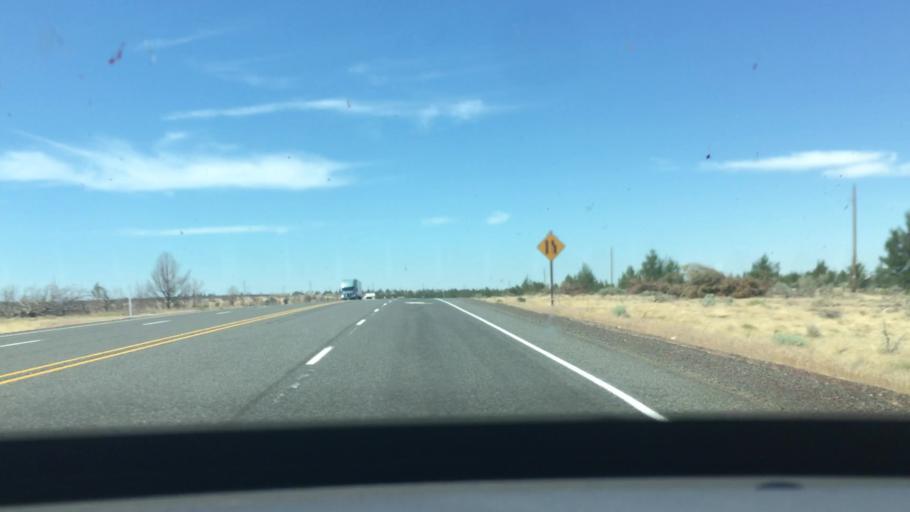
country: US
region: Oregon
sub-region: Jefferson County
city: Madras
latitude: 44.9038
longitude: -120.9382
